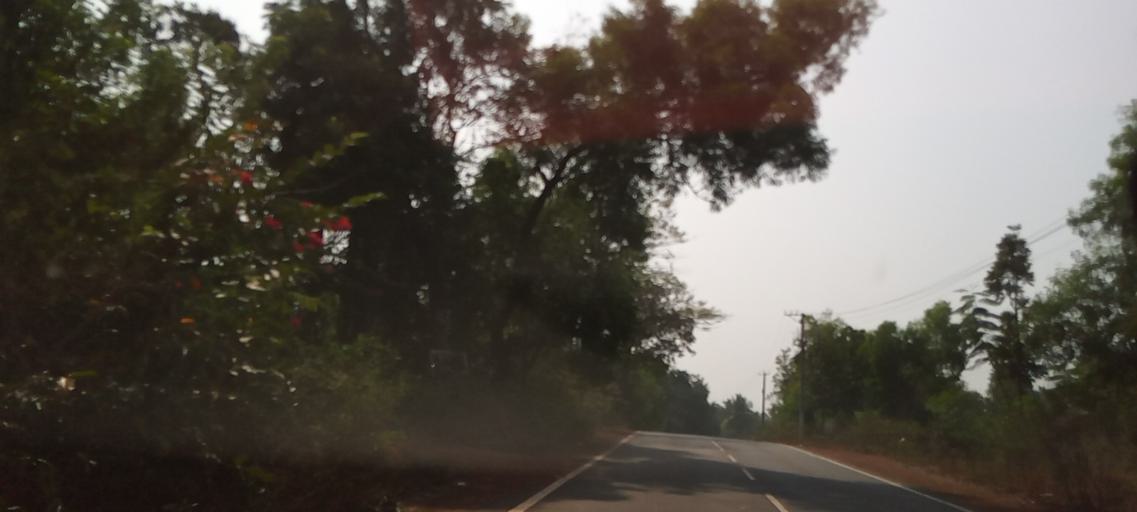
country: IN
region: Karnataka
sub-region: Udupi
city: Someshwar
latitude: 13.5379
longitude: 74.9155
